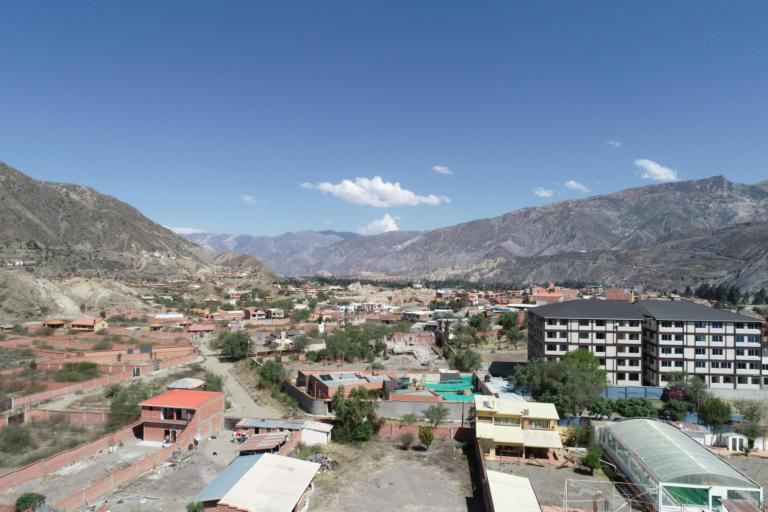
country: BO
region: La Paz
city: La Paz
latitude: -16.6493
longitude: -68.0366
